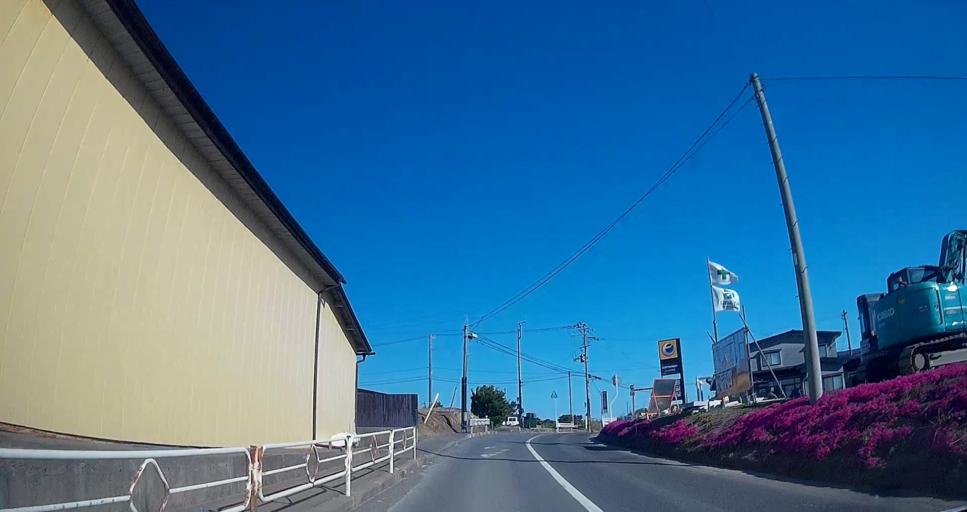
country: JP
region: Aomori
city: Hachinohe
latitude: 40.5105
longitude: 141.6075
